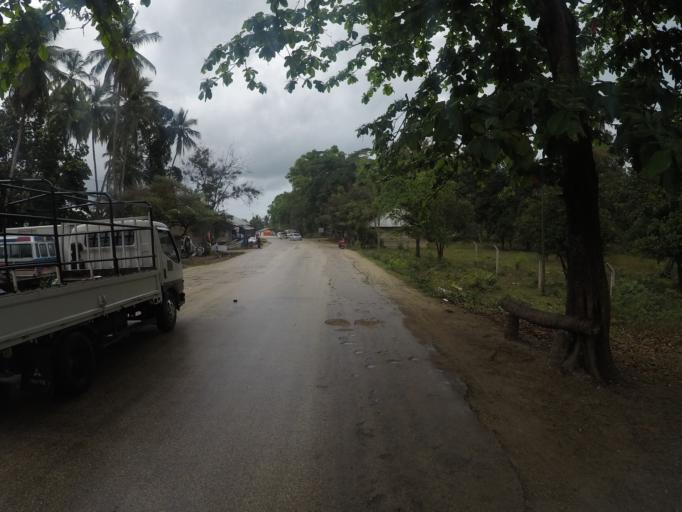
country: TZ
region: Zanzibar Urban/West
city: Zanzibar
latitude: -6.0924
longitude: 39.2194
